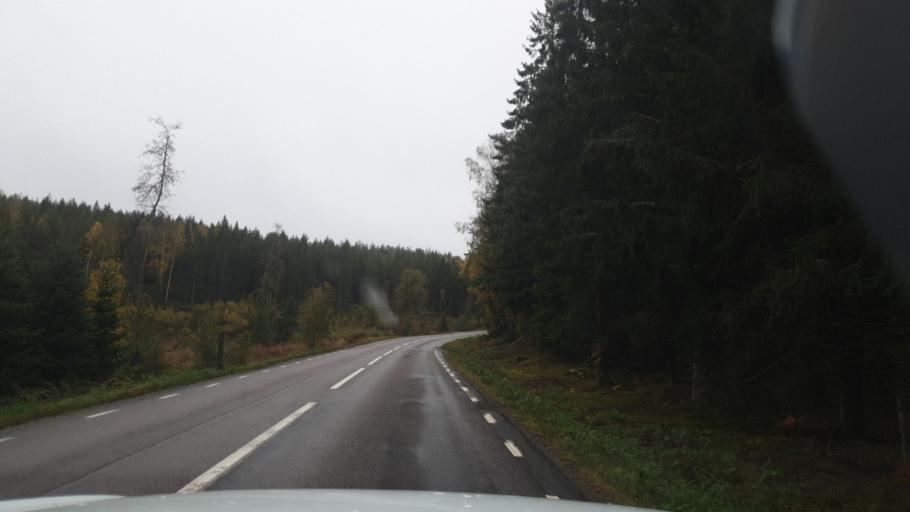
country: SE
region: Vaermland
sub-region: Eda Kommun
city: Amotfors
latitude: 59.6727
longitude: 12.3853
